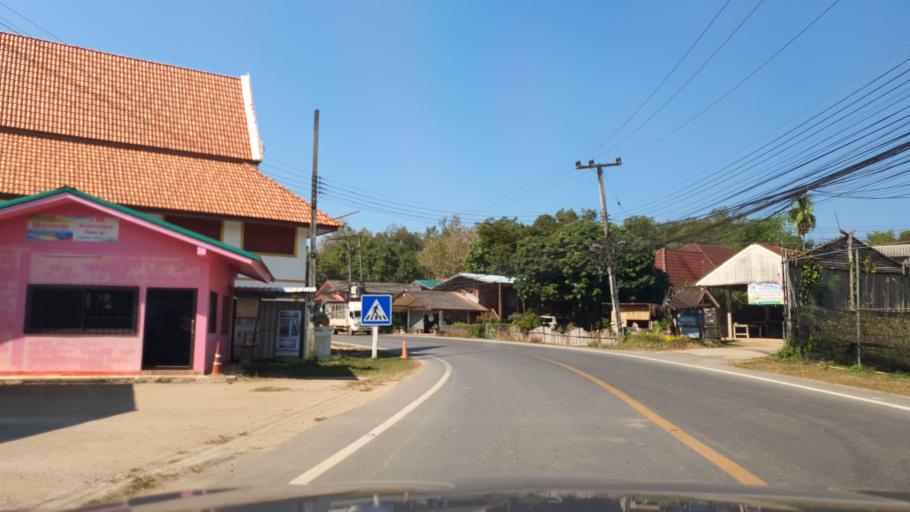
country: TH
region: Nan
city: Tha Wang Pha
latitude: 19.0821
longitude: 100.8802
